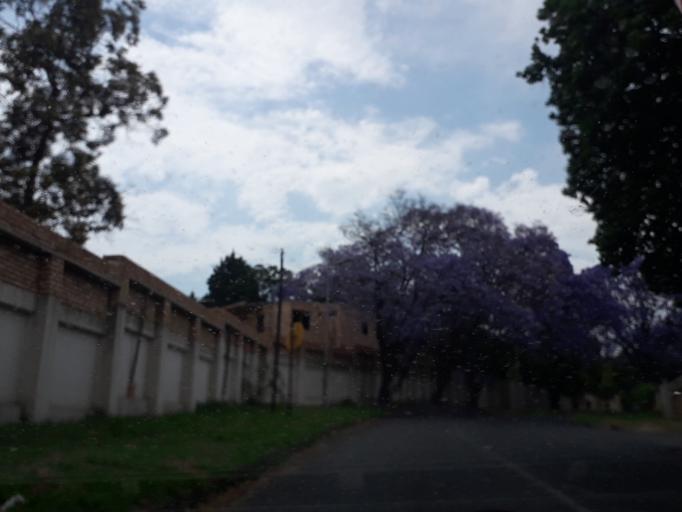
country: ZA
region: Gauteng
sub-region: City of Johannesburg Metropolitan Municipality
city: Johannesburg
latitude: -26.1583
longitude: 28.0673
